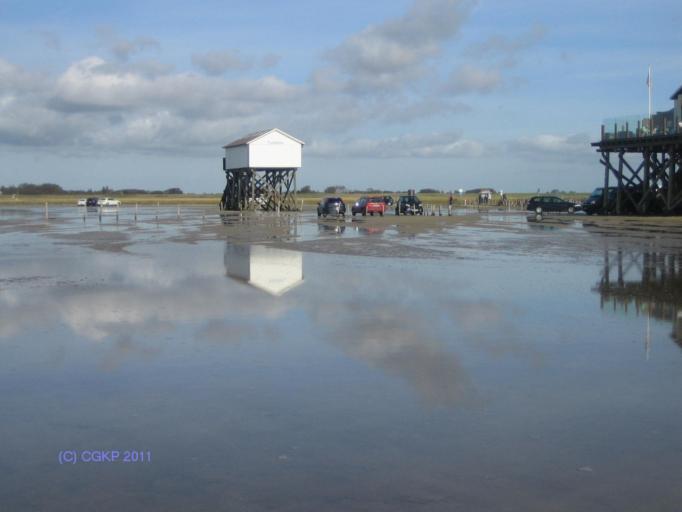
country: DE
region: Schleswig-Holstein
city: Sankt Peter-Ording
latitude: 54.2718
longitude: 8.6536
